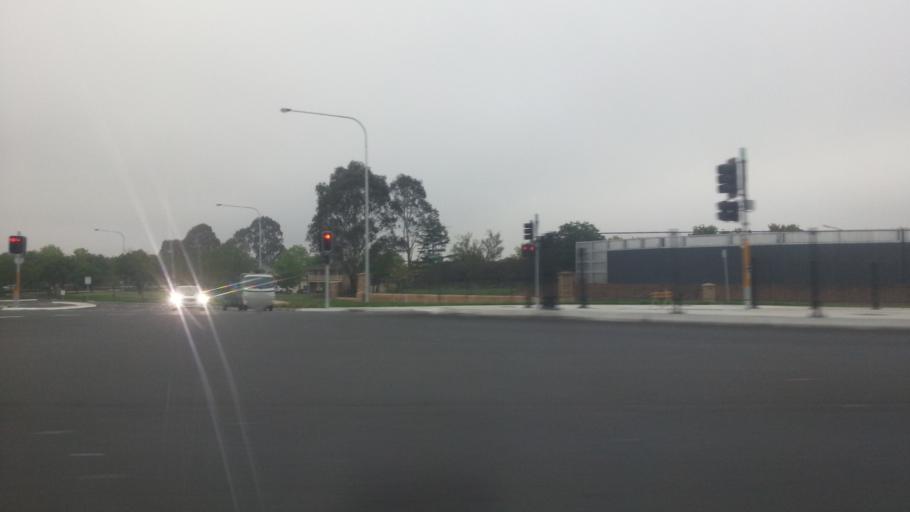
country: AU
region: New South Wales
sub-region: Camden
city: Narellan
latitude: -34.0325
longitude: 150.7297
